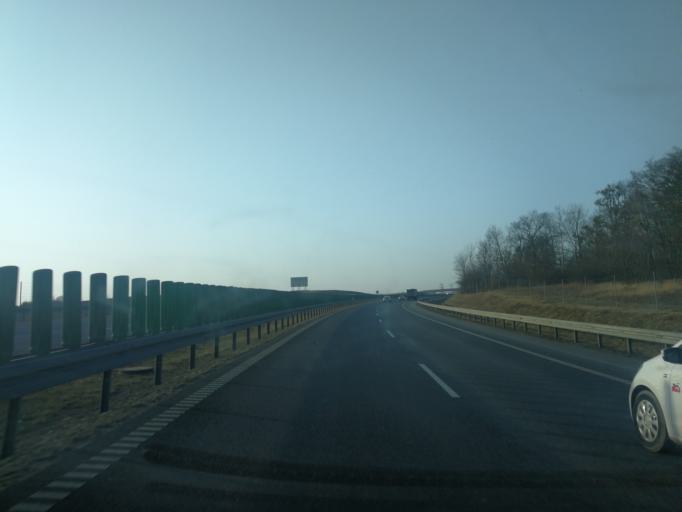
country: PL
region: Warmian-Masurian Voivodeship
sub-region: Powiat elblaski
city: Gronowo Gorne
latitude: 54.1107
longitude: 19.4865
